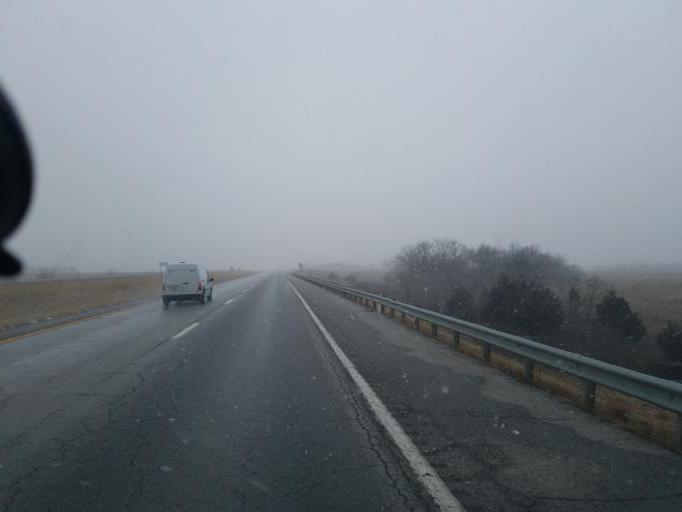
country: US
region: Missouri
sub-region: Macon County
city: La Plata
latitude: 39.9839
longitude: -92.4760
